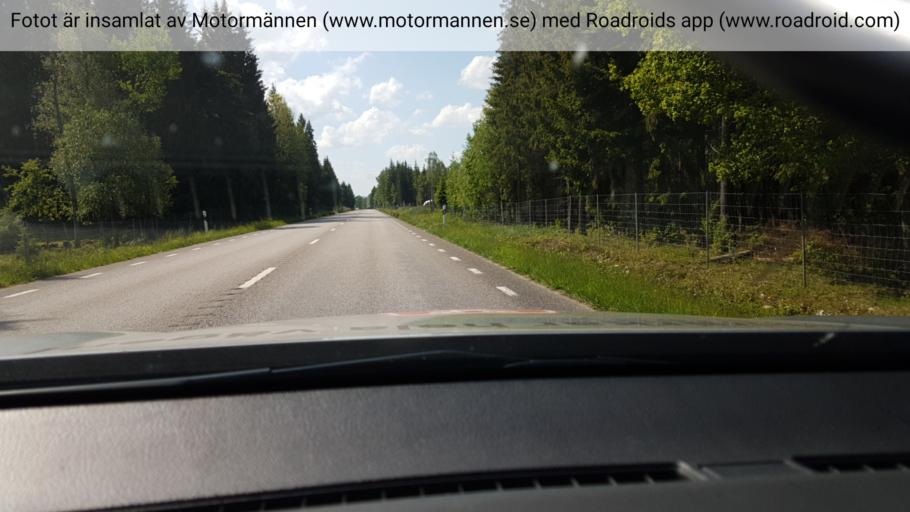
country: SE
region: Vaestra Goetaland
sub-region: Falkopings Kommun
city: Falkoeping
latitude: 58.0393
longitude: 13.5477
